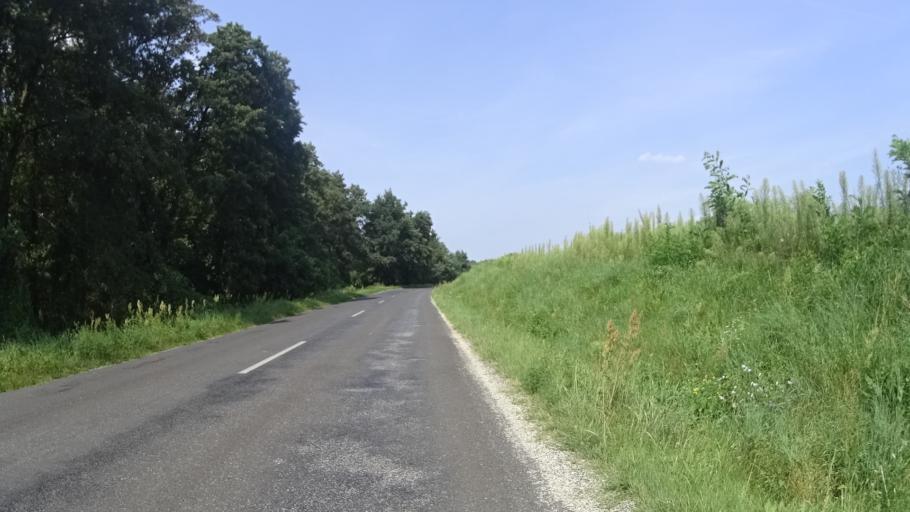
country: HU
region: Zala
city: Murakeresztur
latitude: 46.3877
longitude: 16.9248
